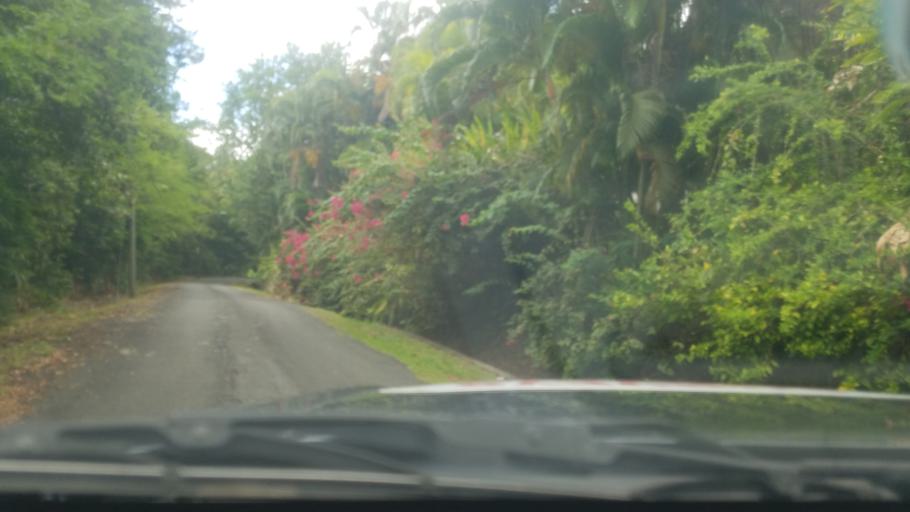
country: LC
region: Praslin
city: Praslin
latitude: 13.8630
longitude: -60.9058
